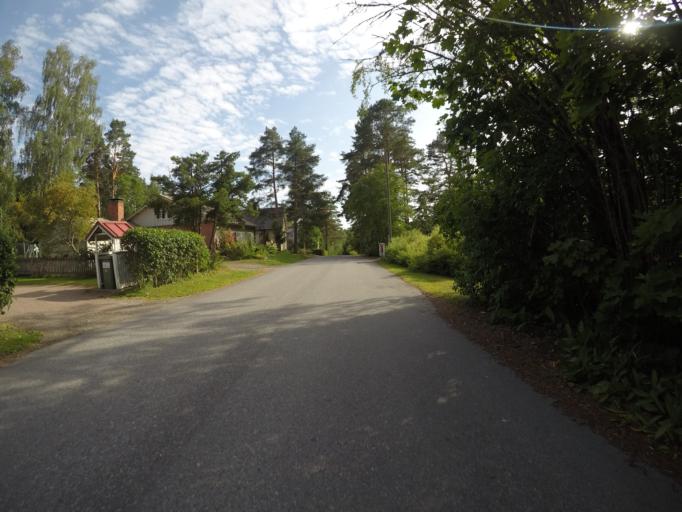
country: FI
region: Haeme
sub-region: Haemeenlinna
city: Haemeenlinna
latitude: 60.9863
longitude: 24.4469
